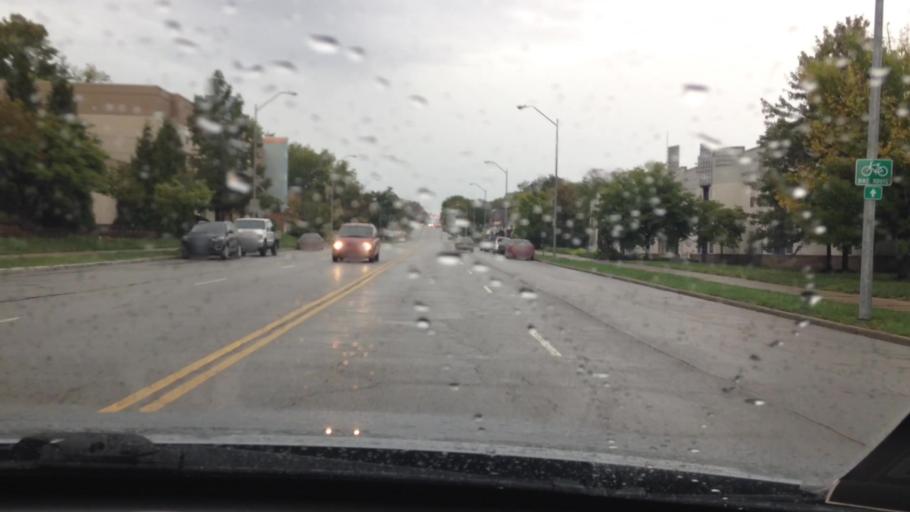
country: US
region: Missouri
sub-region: Jackson County
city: Kansas City
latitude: 39.0509
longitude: -94.5677
